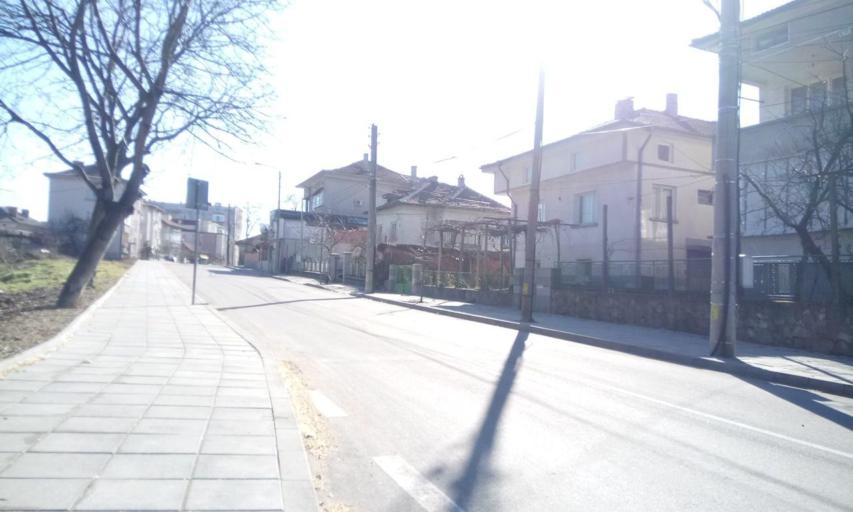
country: BG
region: Plovdiv
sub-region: Obshtina Khisarya
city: Khisarya
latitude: 42.5078
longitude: 24.7136
